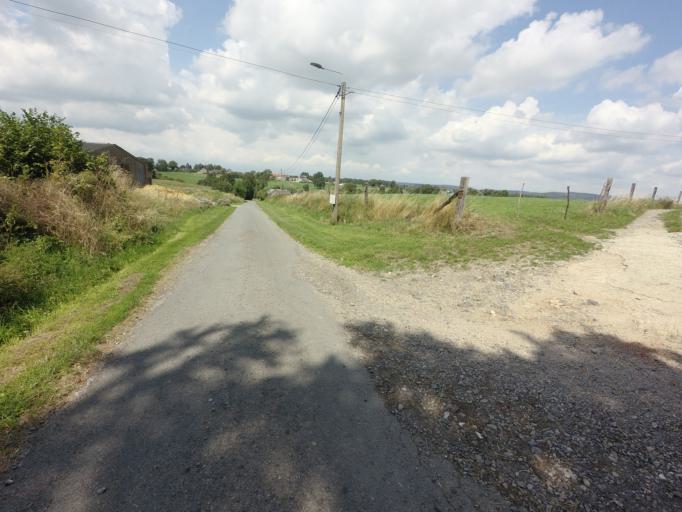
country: BE
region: Wallonia
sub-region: Province de Liege
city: Lontzen
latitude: 50.6979
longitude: 5.9854
